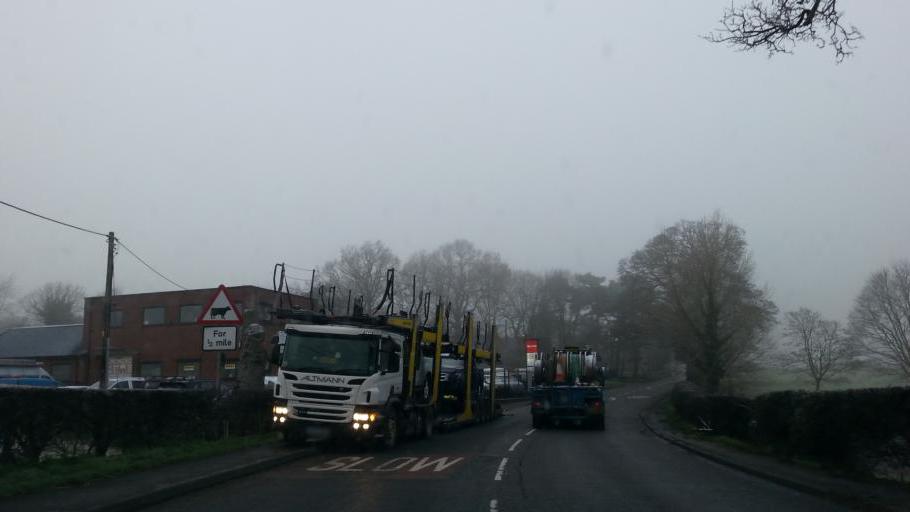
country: GB
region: England
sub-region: Cheshire East
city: Siddington
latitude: 53.2127
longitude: -2.2284
